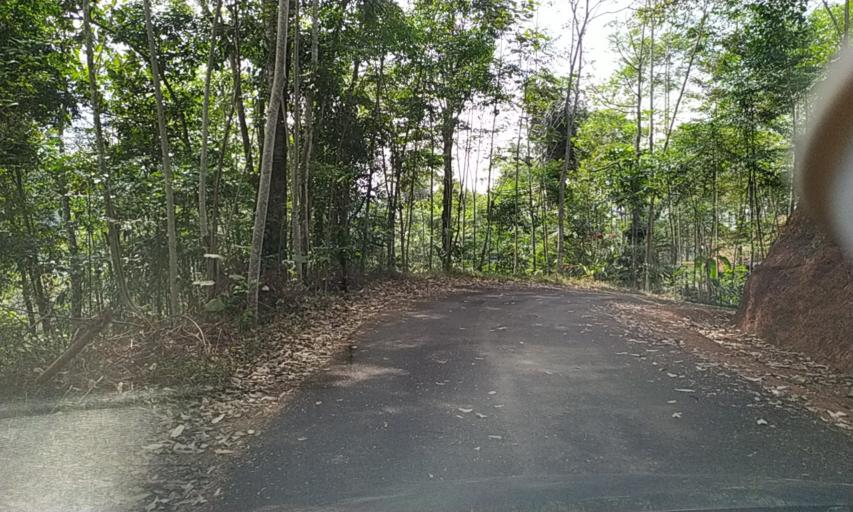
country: ID
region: Central Java
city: Kutaagung
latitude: -7.1818
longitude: 108.5722
